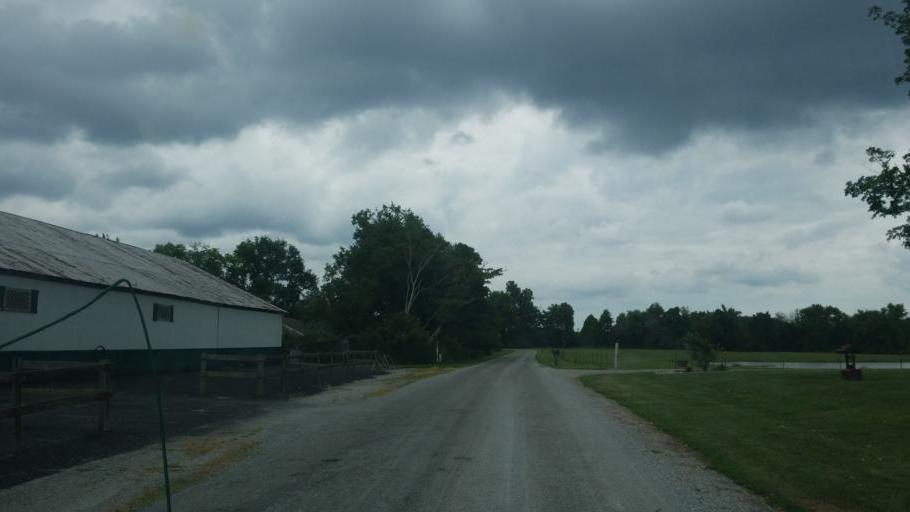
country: US
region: Illinois
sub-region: Jackson County
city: Murphysboro
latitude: 37.7152
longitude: -89.3280
